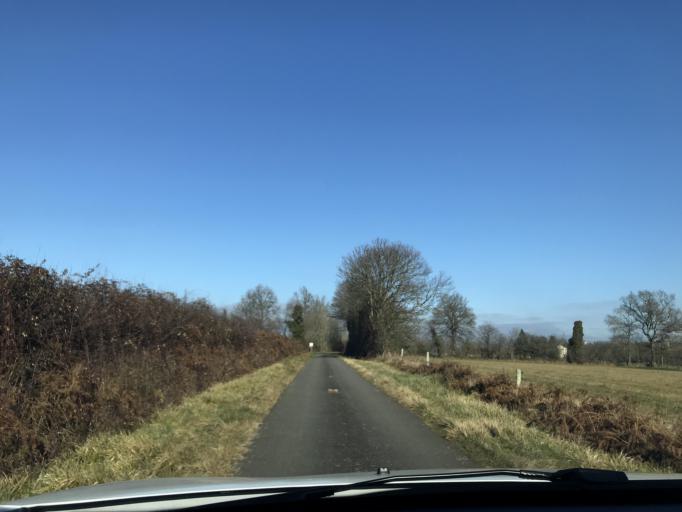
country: FR
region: Poitou-Charentes
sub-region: Departement de la Charente
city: Saint-Claud
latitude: 45.8590
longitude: 0.5321
